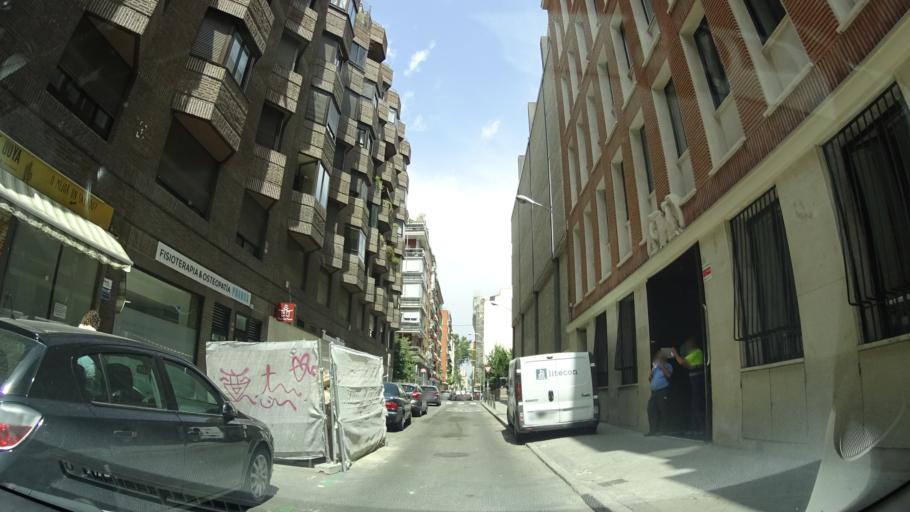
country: ES
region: Madrid
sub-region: Provincia de Madrid
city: Chamberi
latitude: 40.4285
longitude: -3.7171
